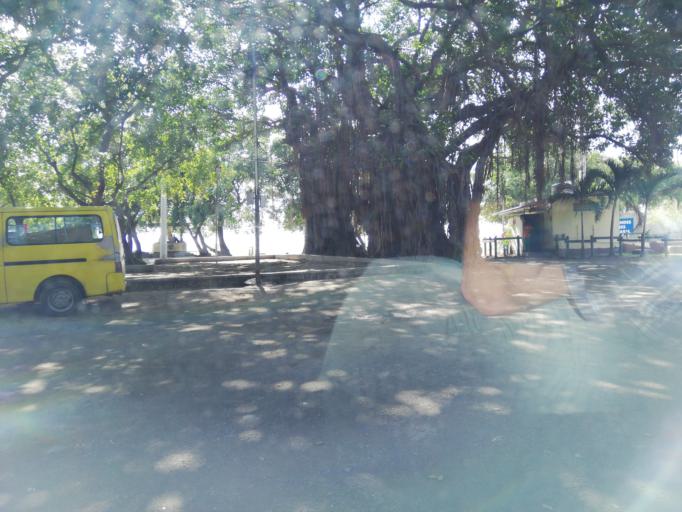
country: MU
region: Port Louis
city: Port Louis
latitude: -20.1603
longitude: 57.4808
